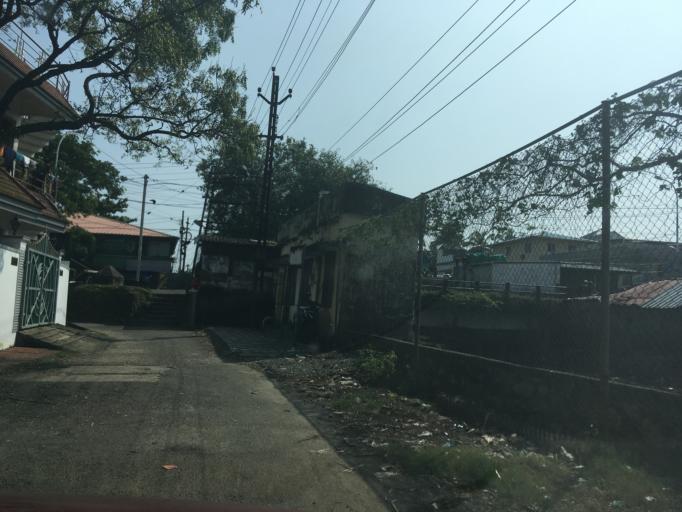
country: IN
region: Kerala
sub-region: Ernakulam
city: Cochin
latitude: 9.9639
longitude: 76.2495
